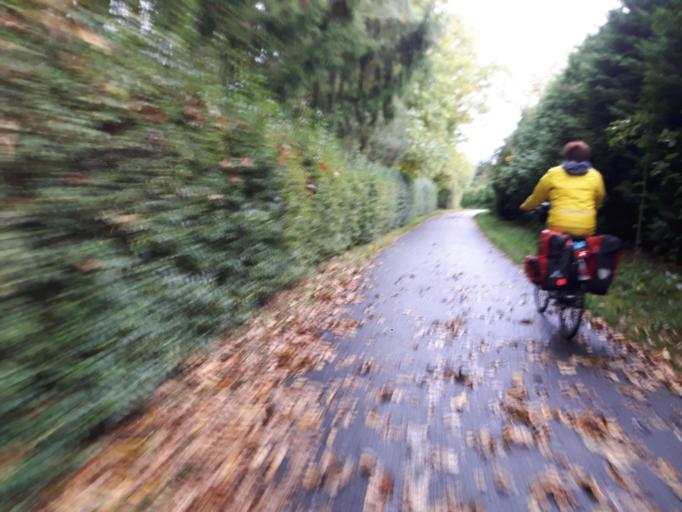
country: DE
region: Bavaria
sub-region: Regierungsbezirk Unterfranken
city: Zellingen
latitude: 49.8900
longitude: 9.8297
